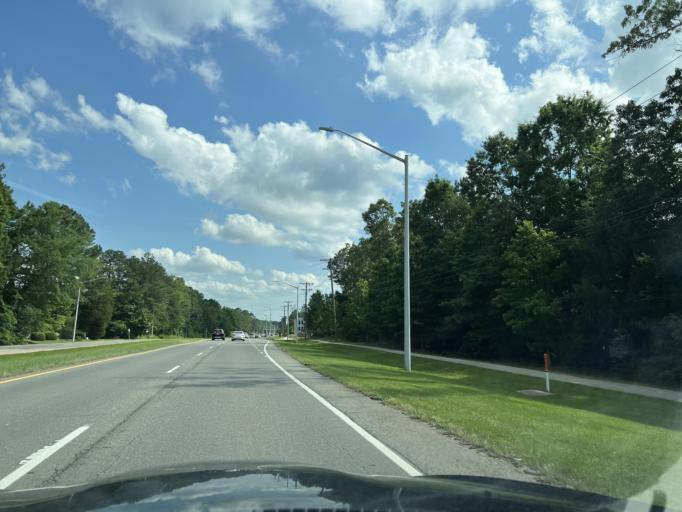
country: US
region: North Carolina
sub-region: Durham County
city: Durham
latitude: 35.9400
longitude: -78.8875
